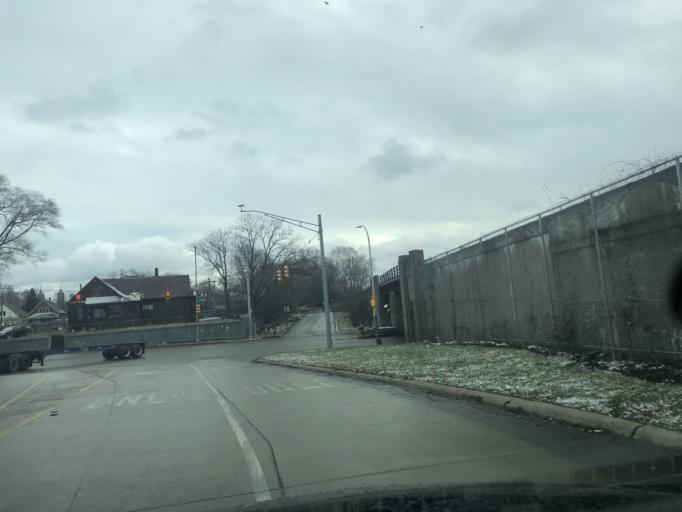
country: US
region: Michigan
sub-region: Wayne County
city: River Rouge
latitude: 42.3242
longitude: -83.1160
